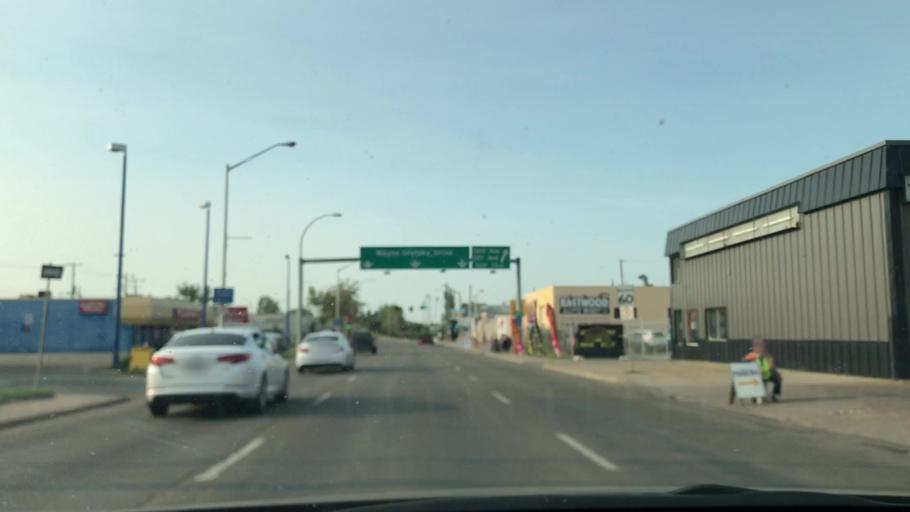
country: CA
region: Alberta
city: Edmonton
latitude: 53.5707
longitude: -113.4522
